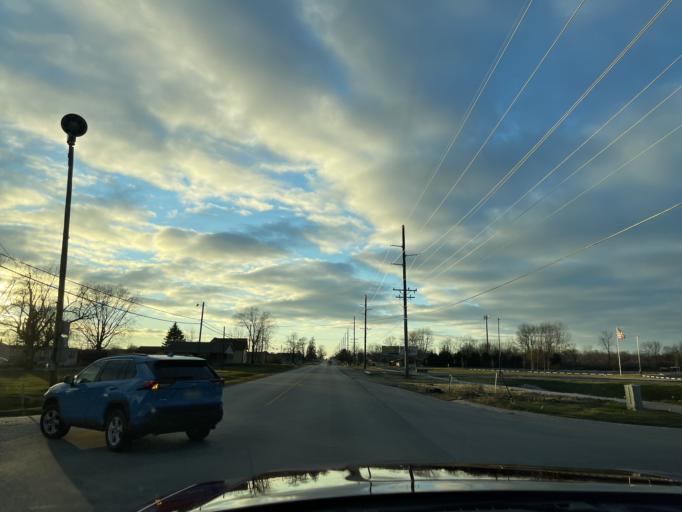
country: US
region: Indiana
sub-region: Hendricks County
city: Avon
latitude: 39.7620
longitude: -86.4571
